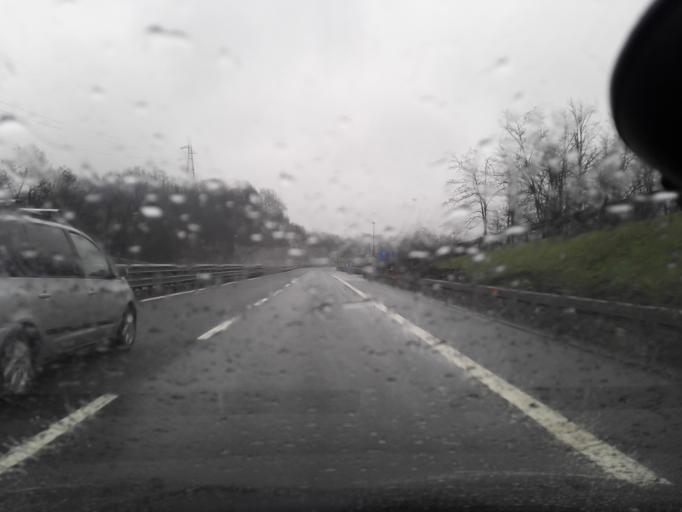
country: IT
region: Piedmont
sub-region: Provincia di Alessandria
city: Vignole Borbera
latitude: 44.7021
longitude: 8.8890
